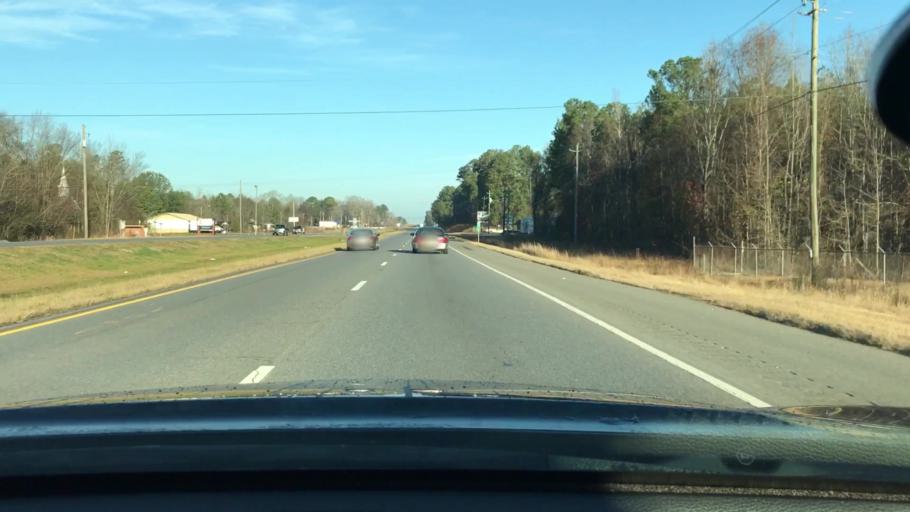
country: US
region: Alabama
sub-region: Talladega County
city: Childersburg
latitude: 33.2365
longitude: -86.3305
